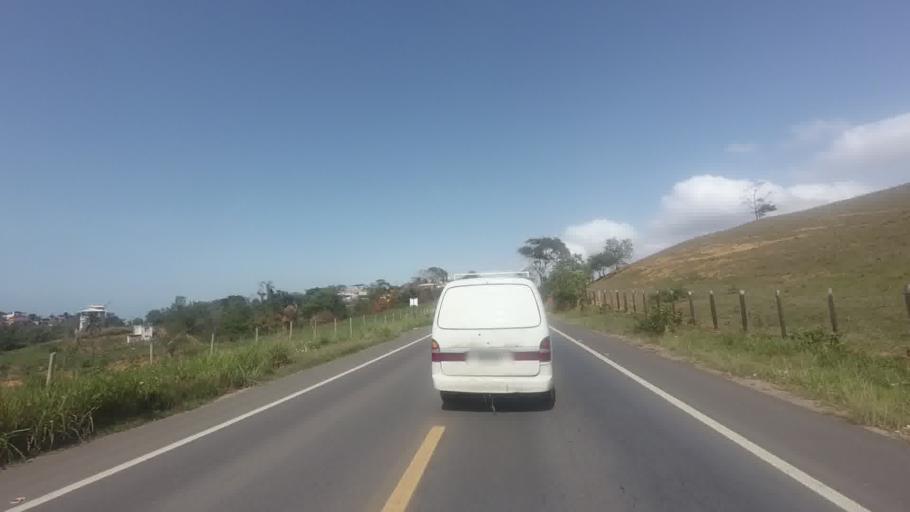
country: BR
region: Espirito Santo
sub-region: Piuma
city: Piuma
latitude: -20.8277
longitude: -40.7008
